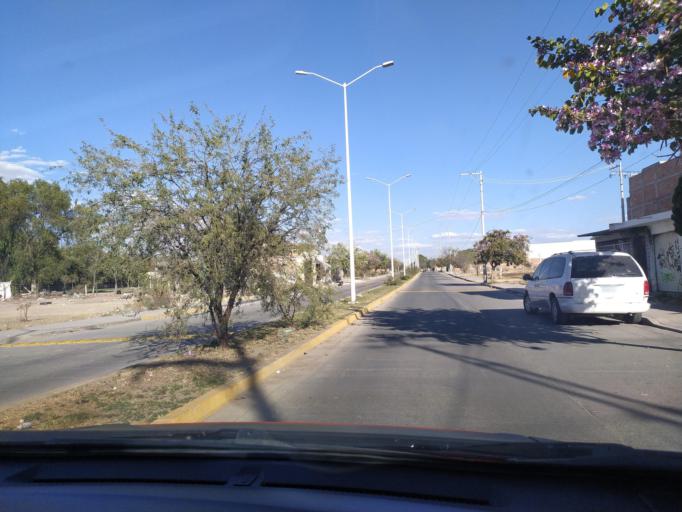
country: LA
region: Oudomxai
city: Muang La
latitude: 21.0174
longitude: 101.8432
